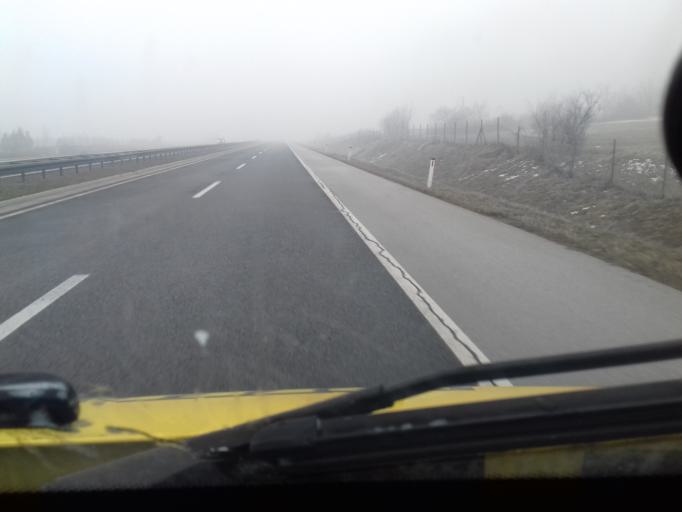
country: BA
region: Federation of Bosnia and Herzegovina
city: Mahala
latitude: 43.9820
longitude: 18.2326
